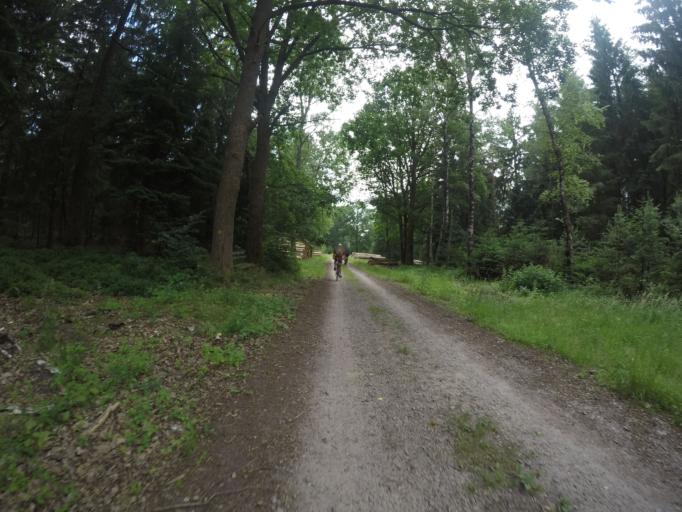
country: DE
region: Lower Saxony
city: Asendorf
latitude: 53.2433
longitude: 9.9599
